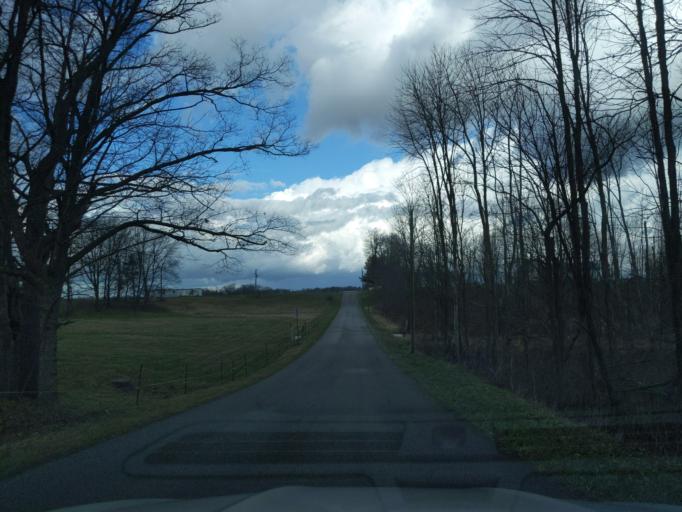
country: US
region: Indiana
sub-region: Decatur County
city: Saint Paul
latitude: 39.3931
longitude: -85.5599
